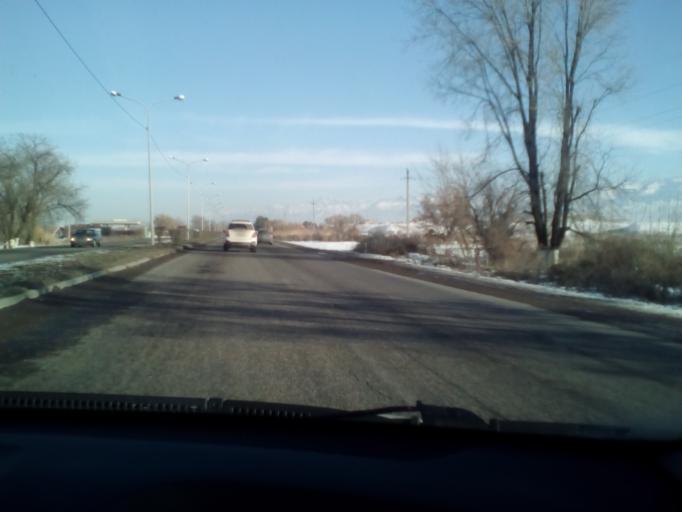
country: KZ
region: Almaty Oblysy
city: Burunday
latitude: 43.2225
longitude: 76.4208
